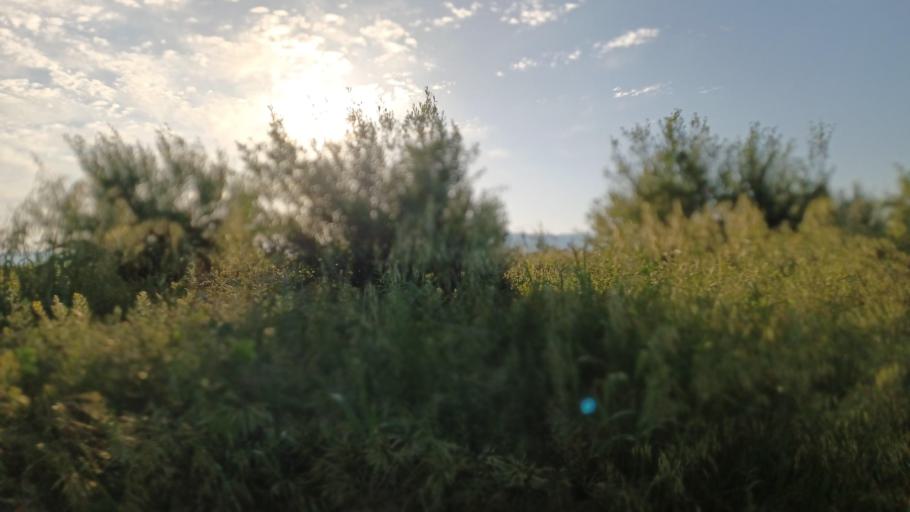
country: CY
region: Pafos
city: Polis
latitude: 35.0251
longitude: 32.4001
